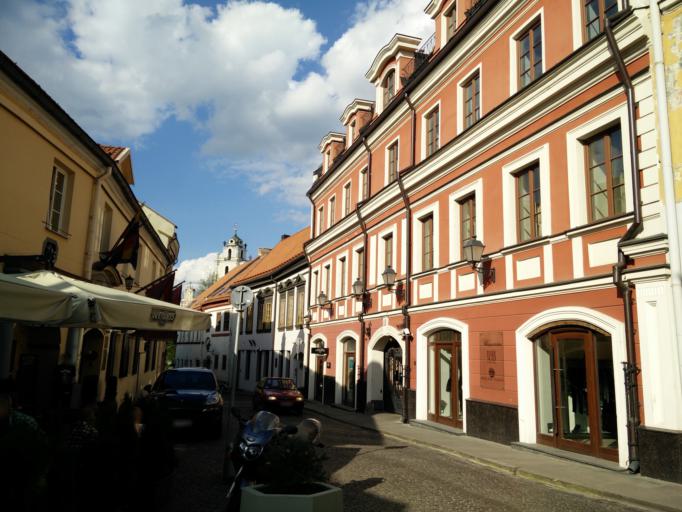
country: LT
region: Vilnius County
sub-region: Vilnius
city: Vilnius
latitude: 54.6804
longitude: 25.2860
